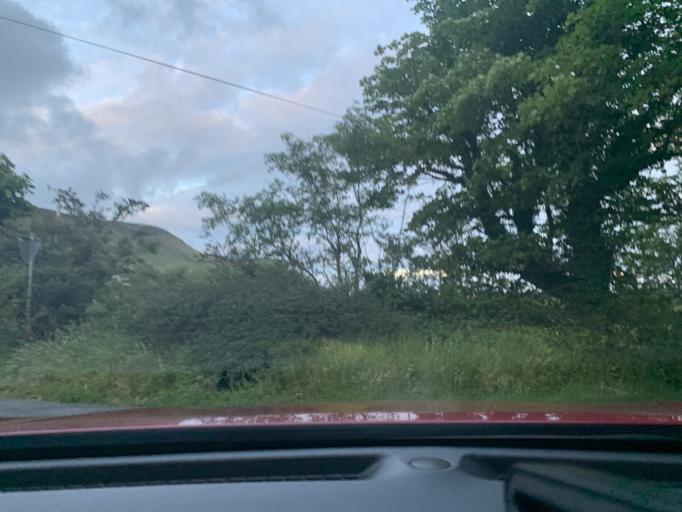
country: IE
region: Connaught
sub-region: Sligo
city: Sligo
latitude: 54.3529
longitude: -8.4881
